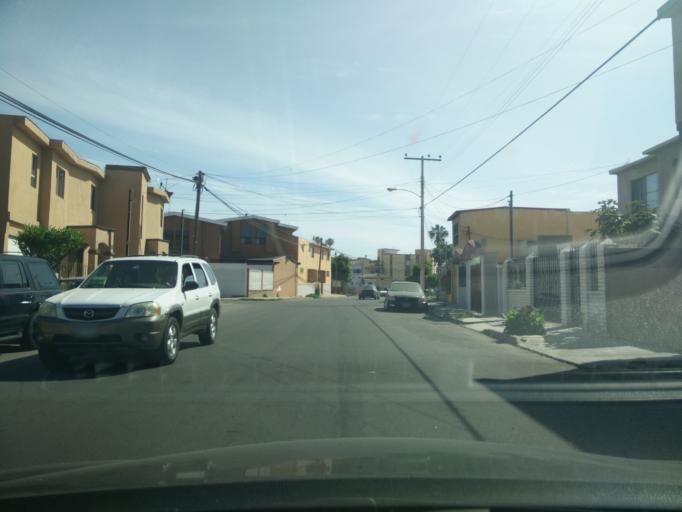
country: MX
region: Baja California
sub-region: Tijuana
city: La Esperanza [Granjas Familiares]
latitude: 32.5077
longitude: -117.1182
